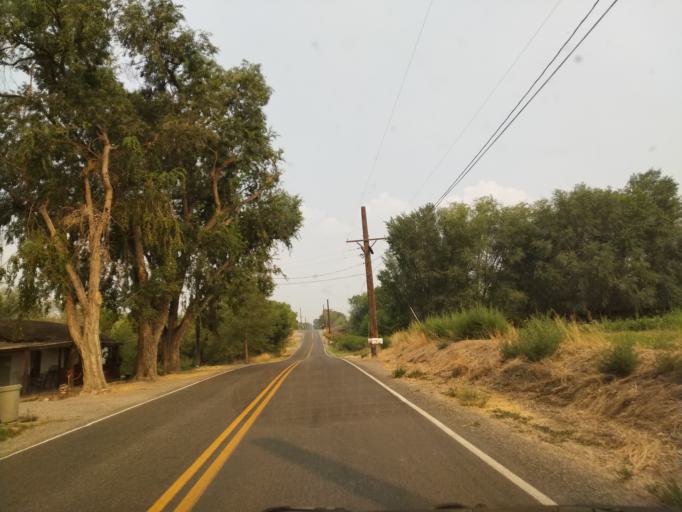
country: US
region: Colorado
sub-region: Mesa County
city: Clifton
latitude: 39.0485
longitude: -108.4628
